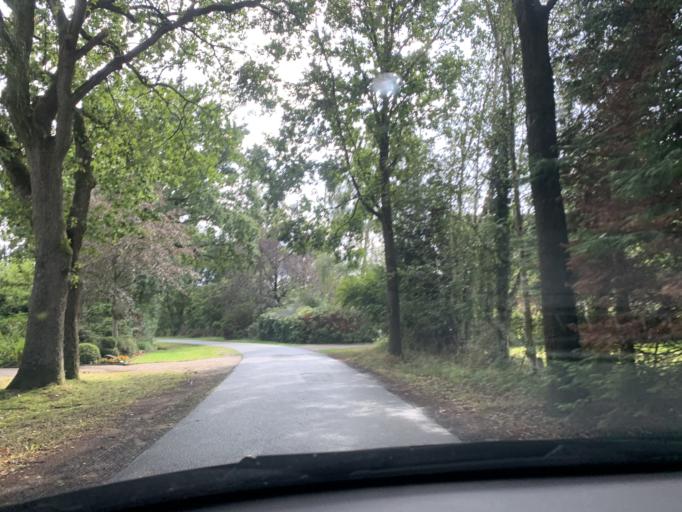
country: DE
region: Lower Saxony
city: Westerstede
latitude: 53.2666
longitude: 7.9000
